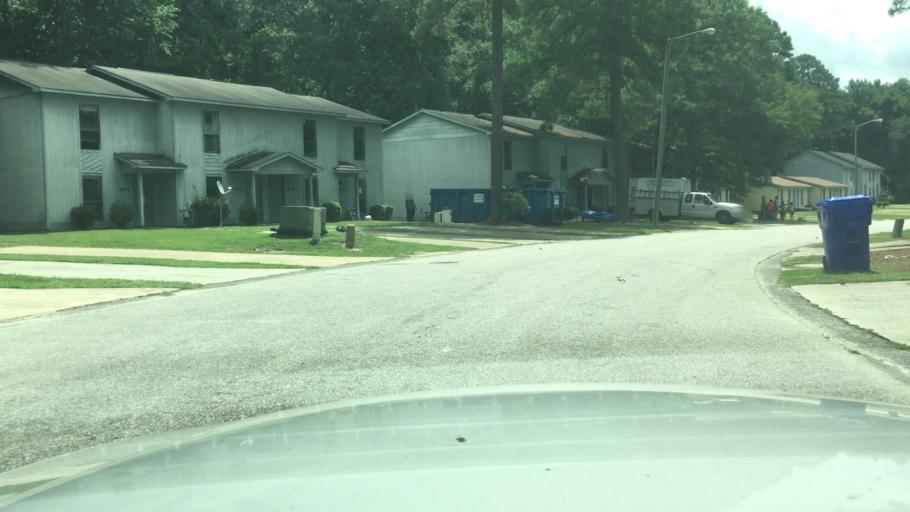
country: US
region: North Carolina
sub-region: Cumberland County
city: Hope Mills
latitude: 35.0355
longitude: -78.9752
